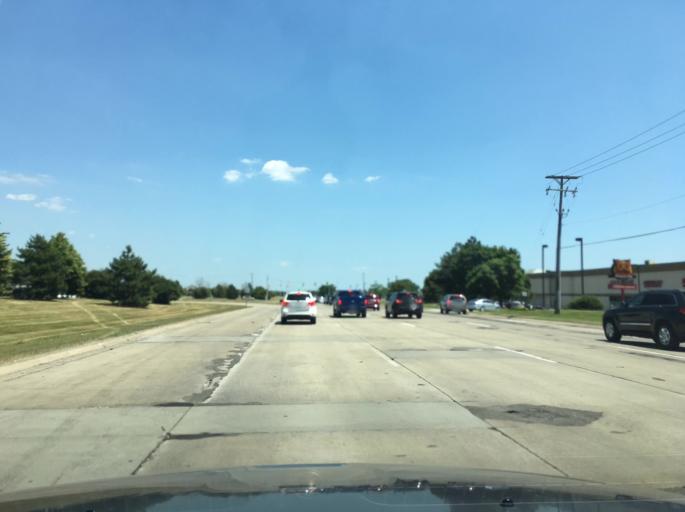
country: US
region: Michigan
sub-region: Macomb County
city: Utica
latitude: 42.6267
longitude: -82.9978
